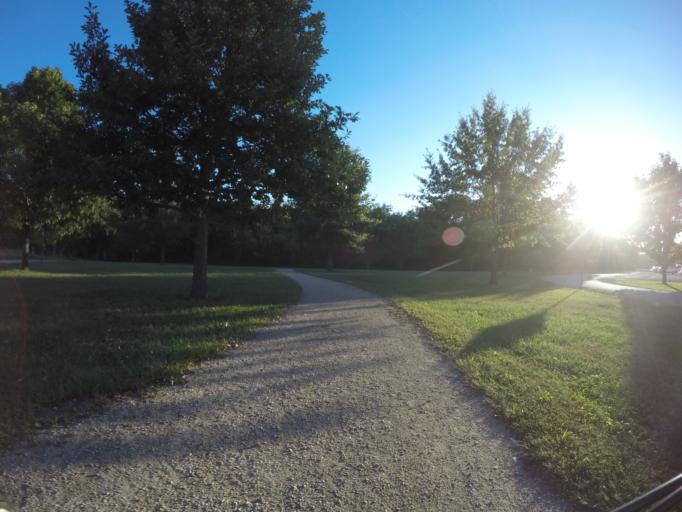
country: US
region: Kansas
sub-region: Riley County
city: Manhattan
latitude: 39.1826
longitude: -96.6292
